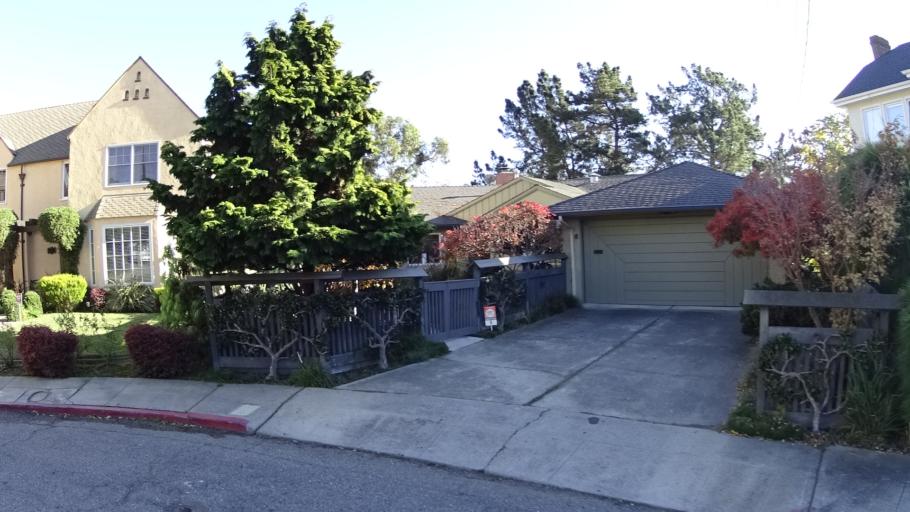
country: US
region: California
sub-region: Alameda County
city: Piedmont
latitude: 37.8107
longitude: -122.2255
